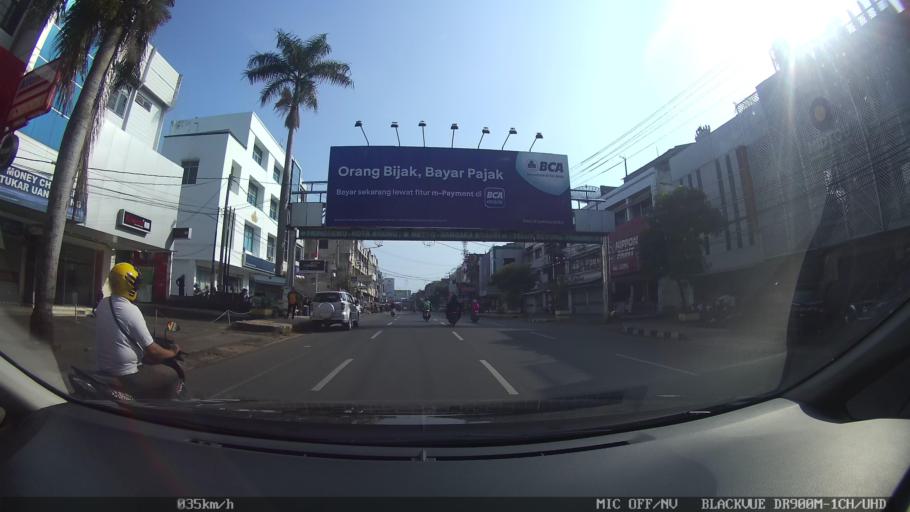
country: ID
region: Lampung
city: Bandarlampung
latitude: -5.4144
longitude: 105.2552
